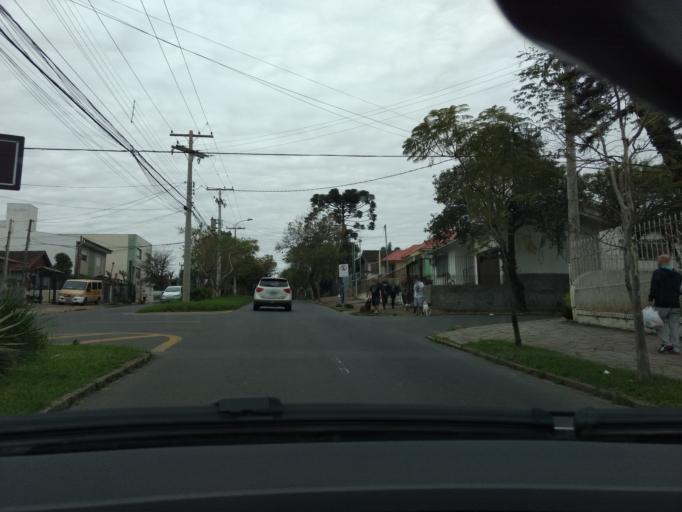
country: BR
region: Rio Grande do Sul
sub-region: Porto Alegre
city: Porto Alegre
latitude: -30.0303
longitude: -51.1397
